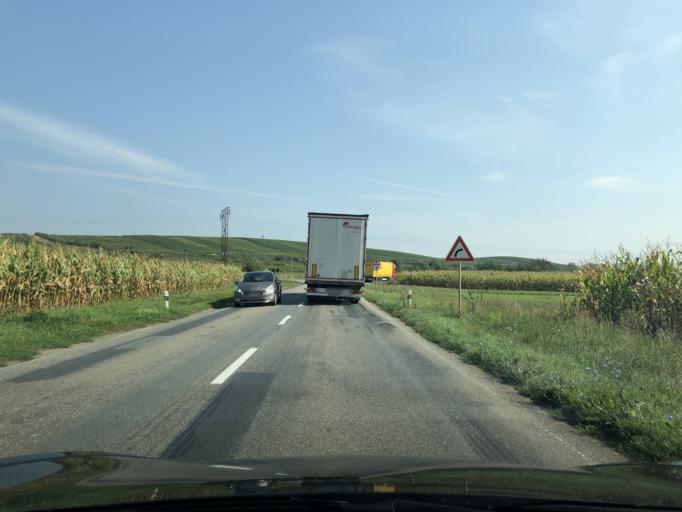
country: CZ
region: South Moravian
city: Brezi
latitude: 48.8209
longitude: 16.5726
